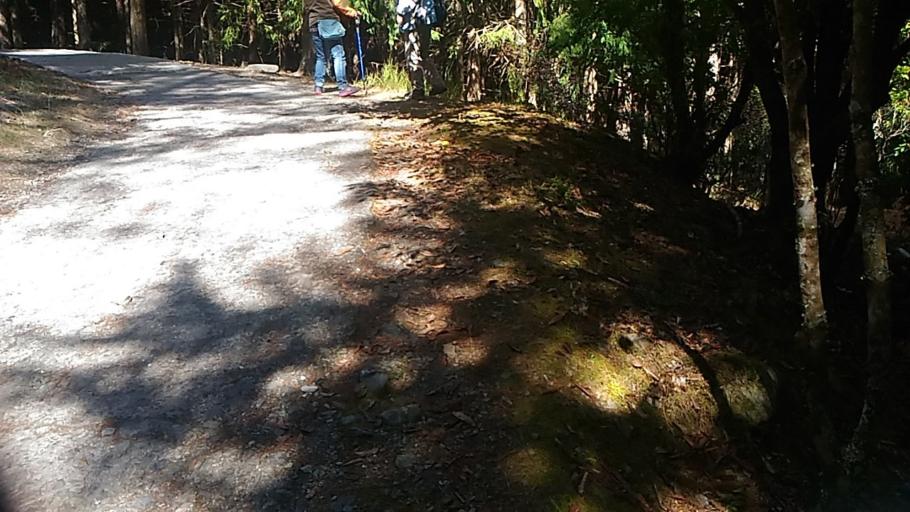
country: TW
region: Taiwan
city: Daxi
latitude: 24.3991
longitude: 121.3082
